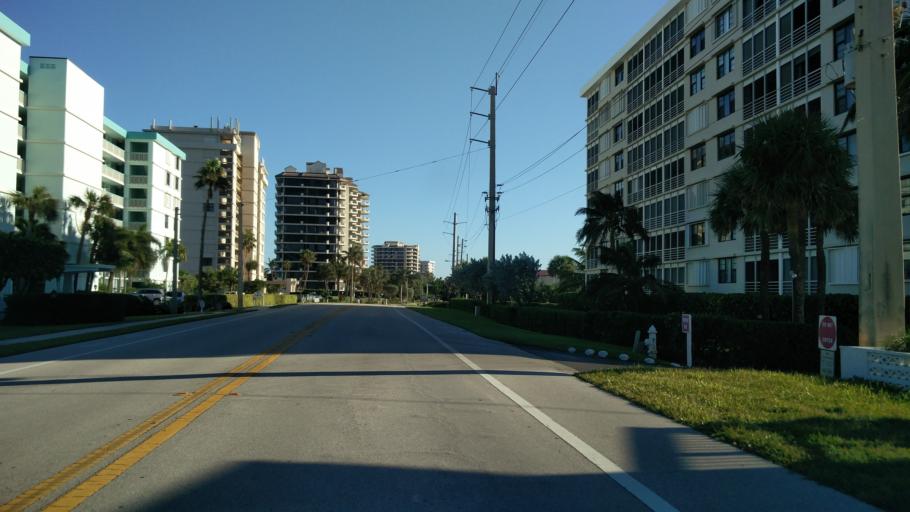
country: US
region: Florida
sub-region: Palm Beach County
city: Juno Beach
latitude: 26.8807
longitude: -80.0535
